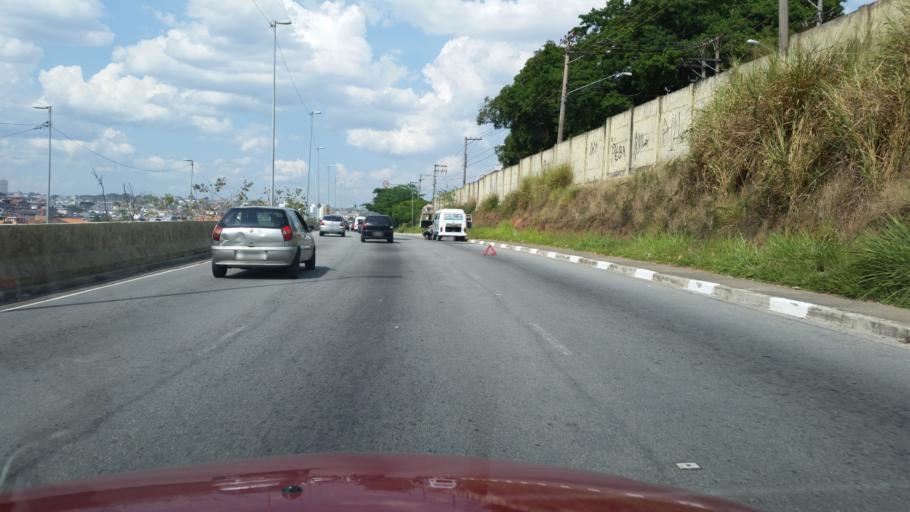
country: BR
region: Sao Paulo
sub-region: Ferraz De Vasconcelos
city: Ferraz de Vasconcelos
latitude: -23.5260
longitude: -46.4376
